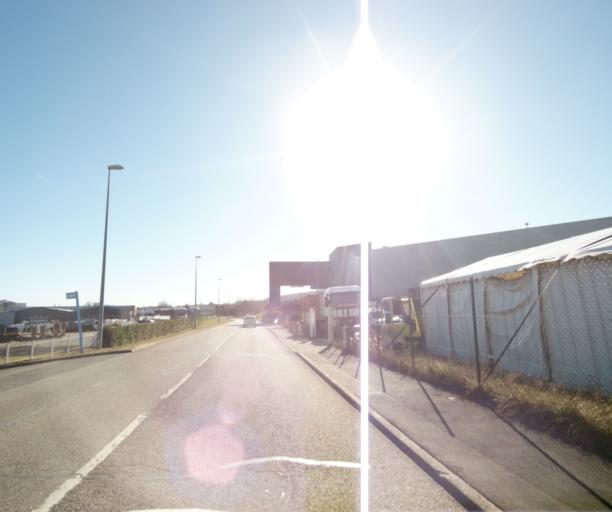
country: FR
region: Lorraine
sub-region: Departement de Meurthe-et-Moselle
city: Vandoeuvre-les-Nancy
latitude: 48.6452
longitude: 6.1852
